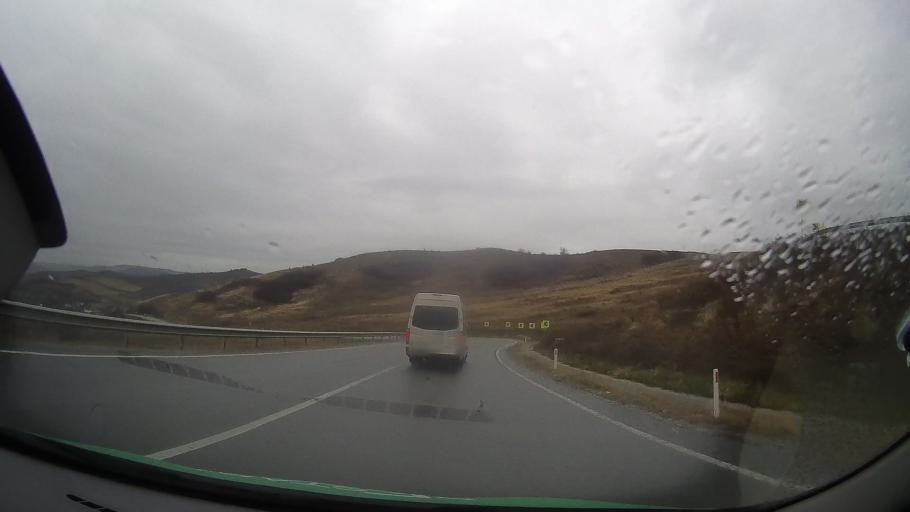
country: RO
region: Bistrita-Nasaud
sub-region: Comuna Galatii Bistritei
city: Galatii Bistritei
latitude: 47.0308
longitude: 24.4230
